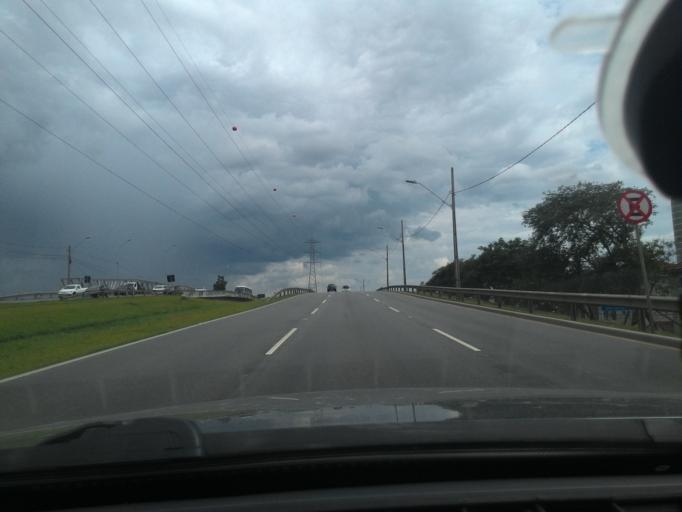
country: BR
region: Parana
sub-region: Sao Jose Dos Pinhais
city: Sao Jose dos Pinhais
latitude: -25.5002
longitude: -49.2095
